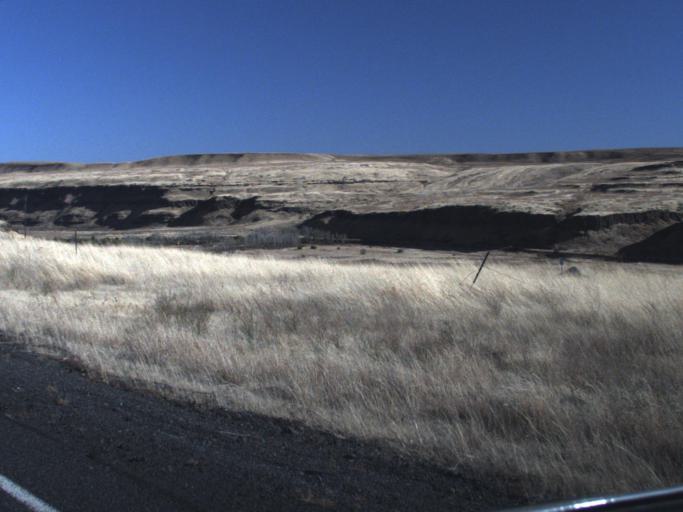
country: US
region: Washington
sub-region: Franklin County
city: Connell
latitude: 46.6508
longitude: -118.5237
